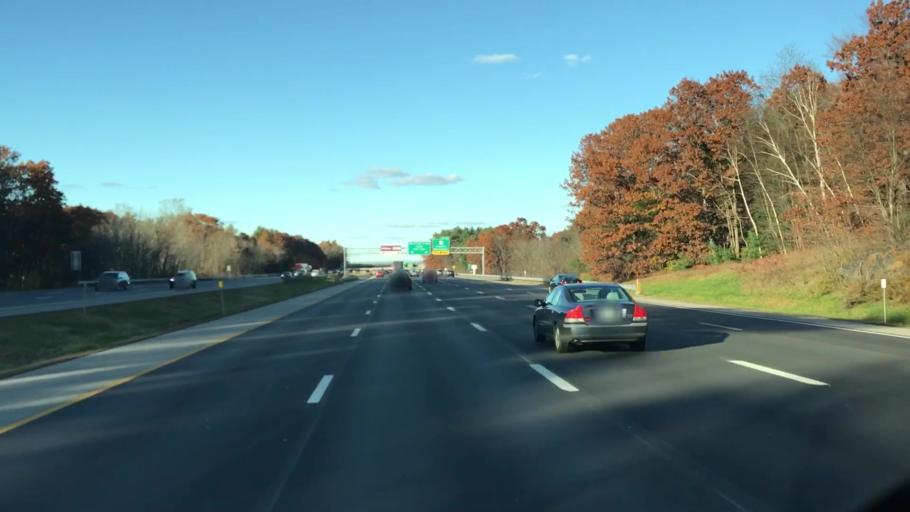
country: US
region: New Hampshire
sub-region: Rockingham County
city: Hampton
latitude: 42.9491
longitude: -70.8589
